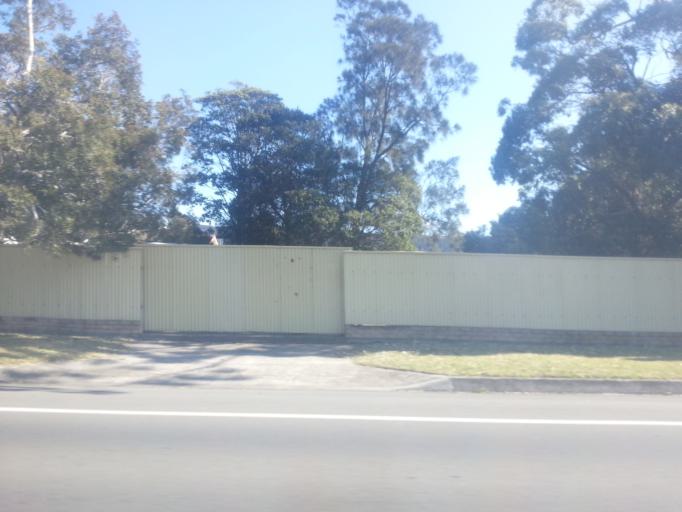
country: AU
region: New South Wales
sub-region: Wollongong
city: East Corrimal
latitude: -34.3647
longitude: 150.9110
